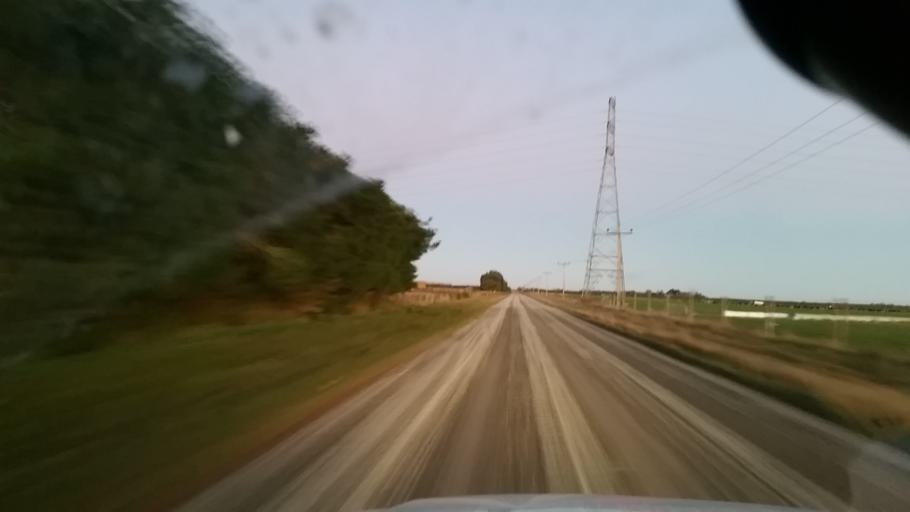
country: NZ
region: Canterbury
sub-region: Ashburton District
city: Tinwald
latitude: -43.9831
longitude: 171.6496
